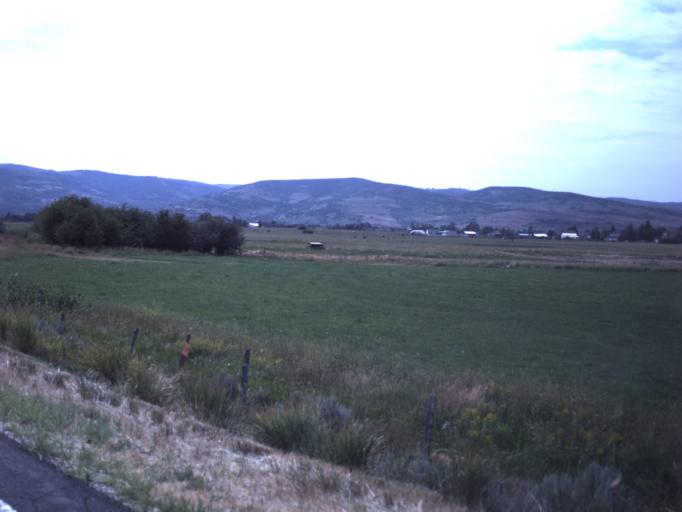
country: US
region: Utah
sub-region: Summit County
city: Francis
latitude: 40.6081
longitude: -111.2571
